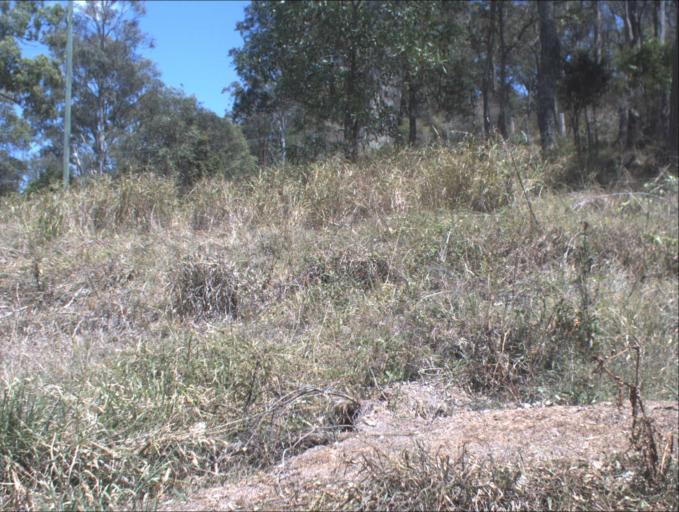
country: AU
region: Queensland
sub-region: Logan
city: Windaroo
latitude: -27.7519
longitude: 153.1807
